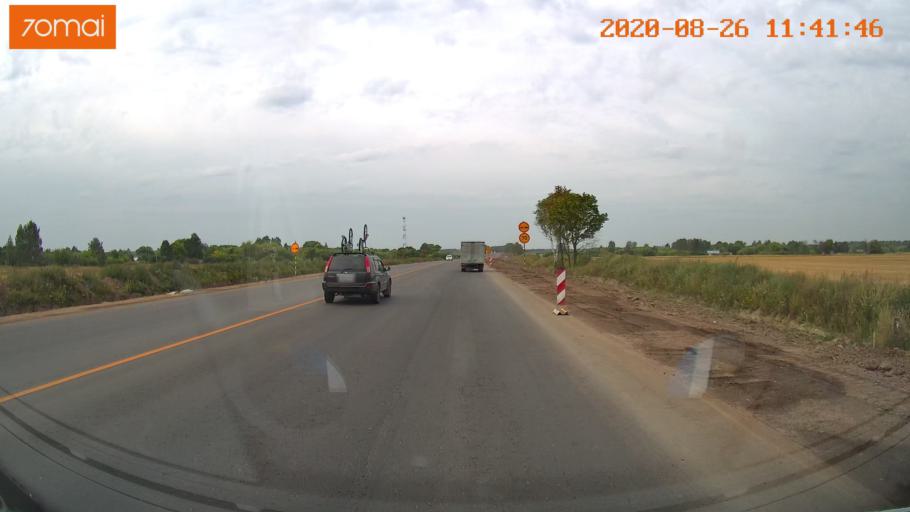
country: RU
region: Rjazan
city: Shilovo
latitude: 54.2958
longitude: 40.7049
